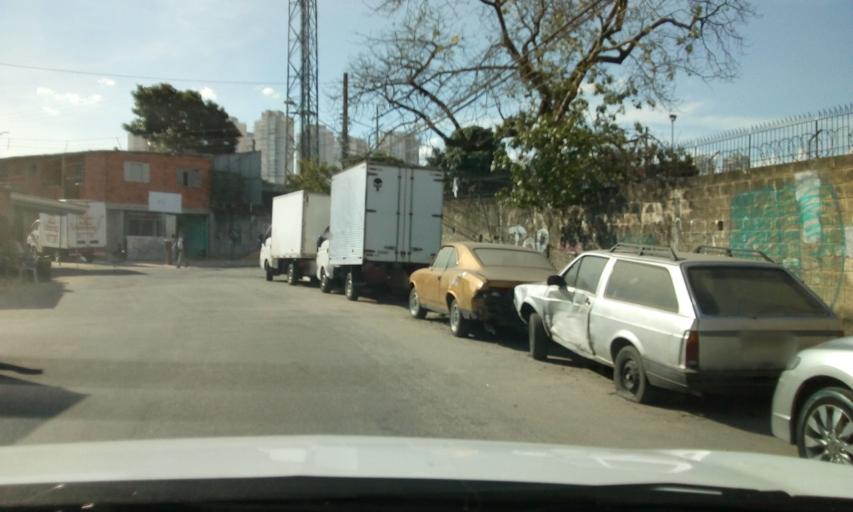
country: BR
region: Sao Paulo
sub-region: Osasco
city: Osasco
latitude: -23.5390
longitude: -46.7319
